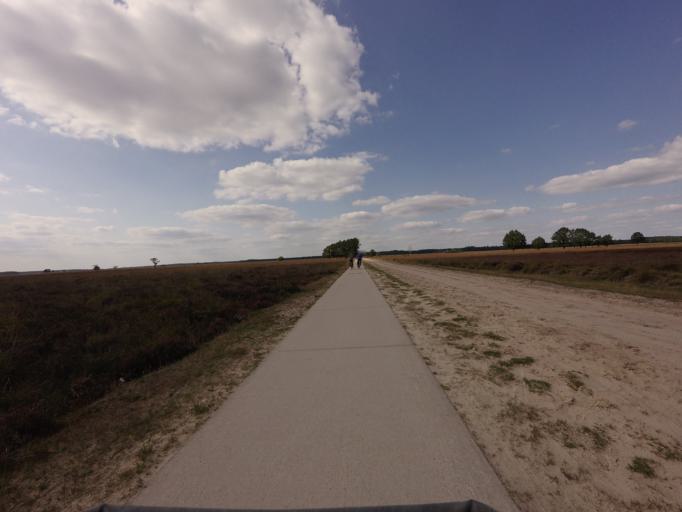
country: NL
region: Drenthe
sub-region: Gemeente Westerveld
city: Dwingeloo
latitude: 52.7985
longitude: 6.4255
